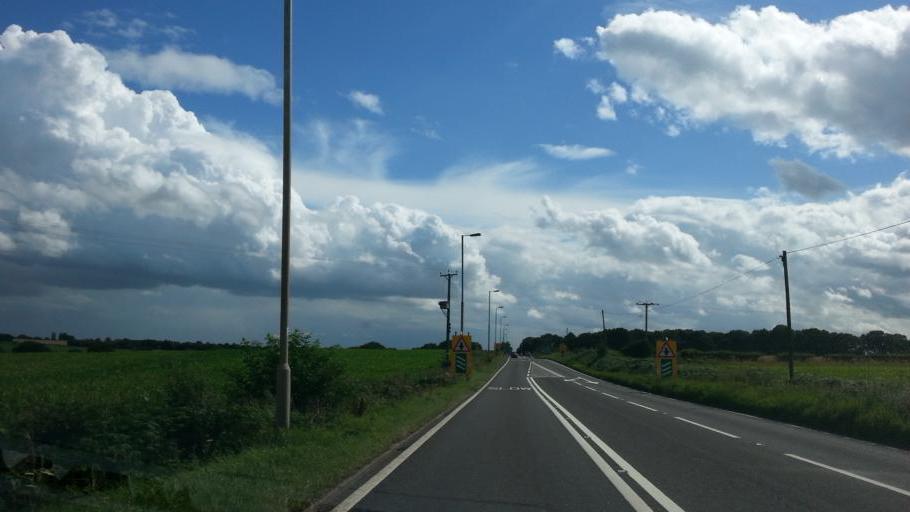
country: GB
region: England
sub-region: Nottinghamshire
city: Bilsthorpe
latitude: 53.1555
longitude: -1.0468
